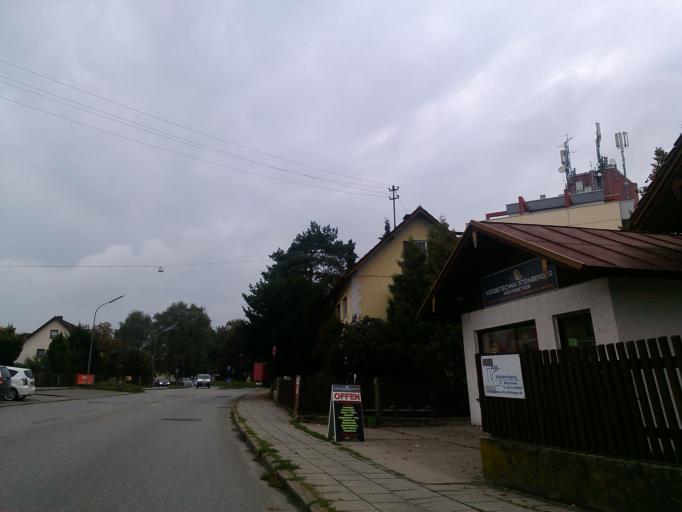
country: DE
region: Bavaria
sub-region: Upper Bavaria
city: Olching
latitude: 48.2040
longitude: 11.3247
